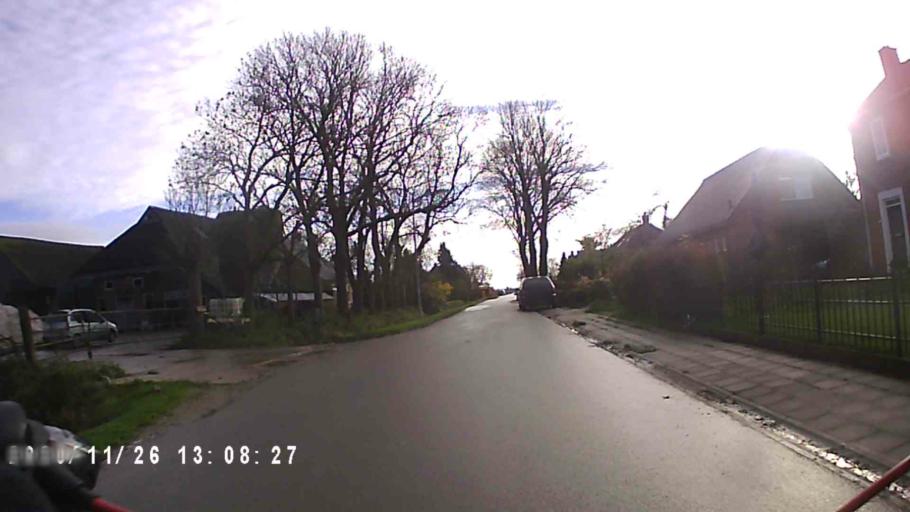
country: NL
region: Groningen
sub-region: Gemeente Appingedam
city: Appingedam
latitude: 53.3537
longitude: 6.8496
